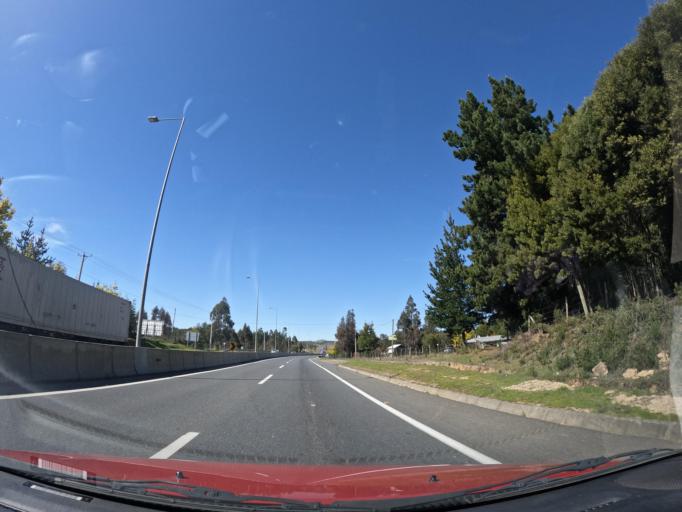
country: CL
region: Biobio
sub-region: Provincia de Concepcion
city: Chiguayante
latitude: -36.9050
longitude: -72.7831
